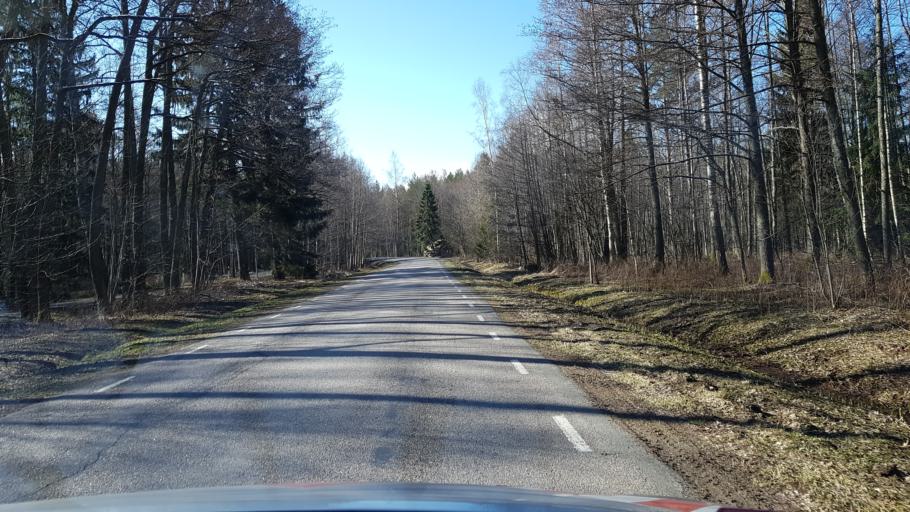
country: EE
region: Harju
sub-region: Loksa linn
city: Loksa
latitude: 59.5936
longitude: 25.9103
